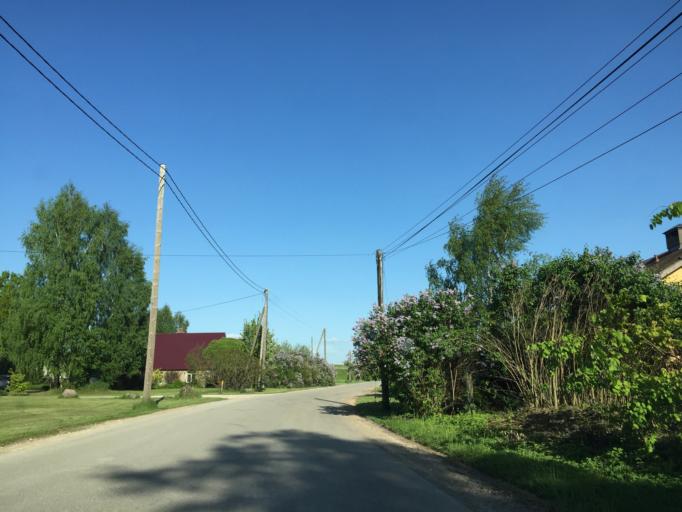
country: LV
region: Kekava
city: Kekava
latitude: 56.8255
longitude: 24.2682
